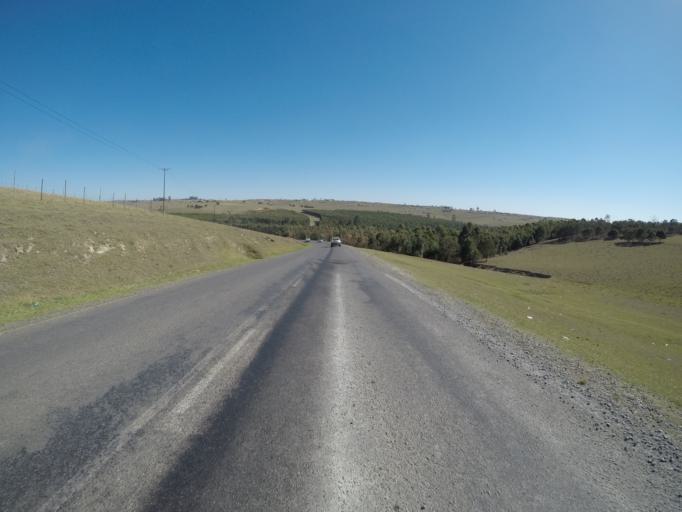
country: ZA
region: Eastern Cape
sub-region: OR Tambo District Municipality
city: Mthatha
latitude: -31.7804
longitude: 28.7381
